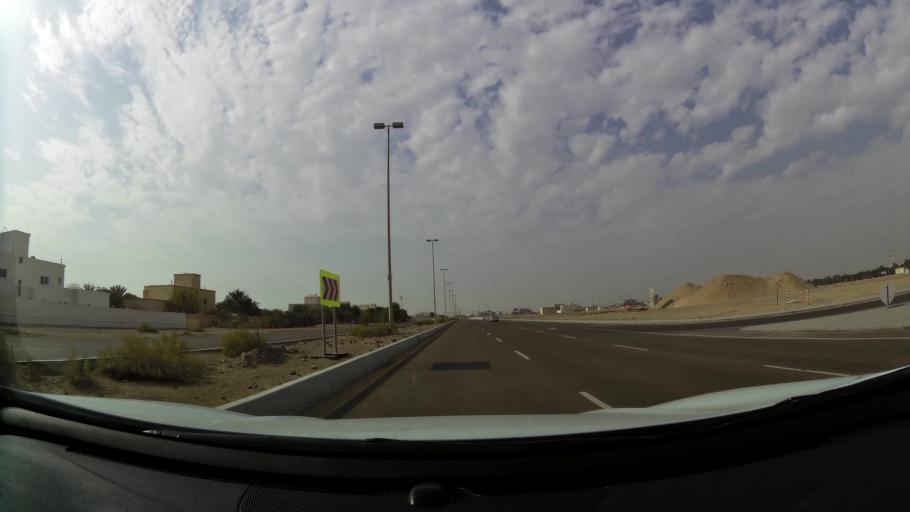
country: AE
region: Abu Dhabi
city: Abu Dhabi
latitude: 24.3351
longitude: 54.5728
